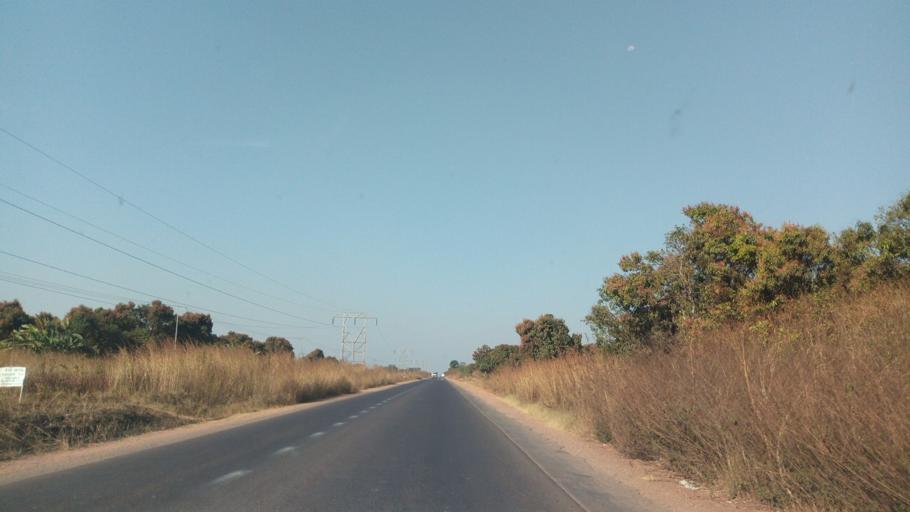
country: CD
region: Katanga
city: Likasi
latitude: -11.0022
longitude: 26.8579
